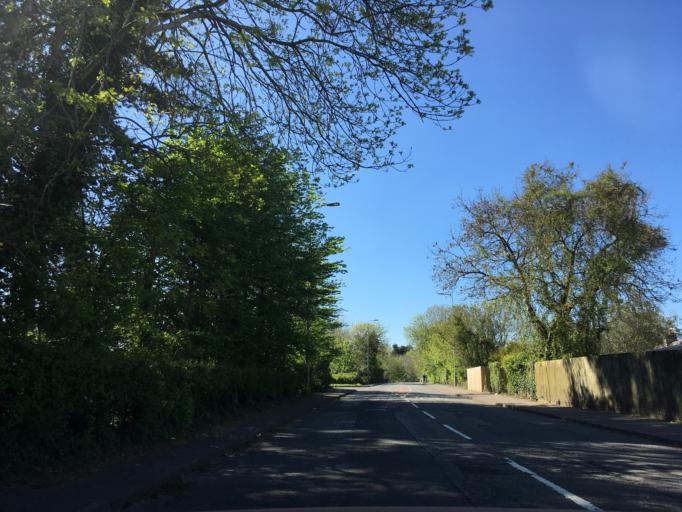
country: GB
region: Wales
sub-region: Cardiff
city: Radyr
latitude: 51.5192
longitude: -3.2305
